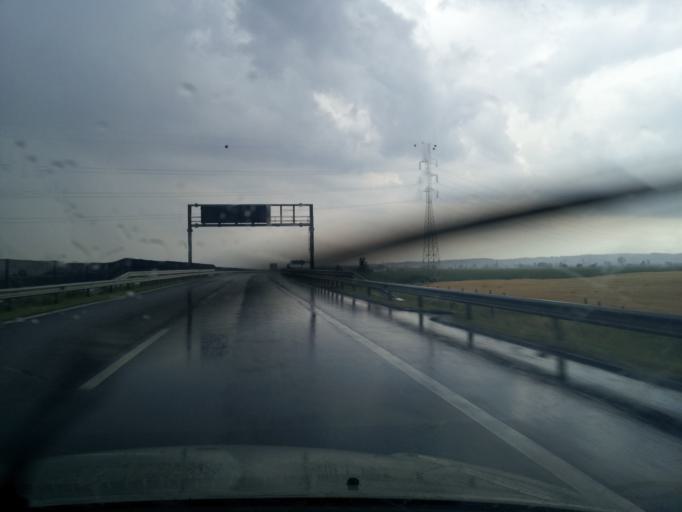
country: HU
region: Borsod-Abauj-Zemplen
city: Alsozsolca
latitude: 48.0727
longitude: 20.8491
